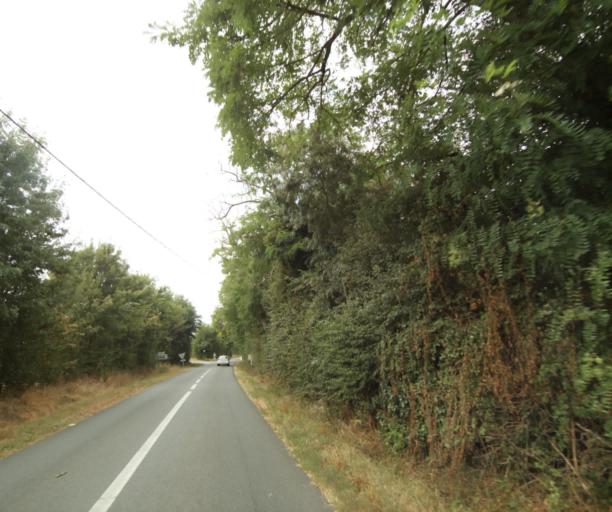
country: FR
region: Poitou-Charentes
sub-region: Departement de la Charente-Maritime
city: Tonnay-Charente
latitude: 45.9515
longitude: -0.8736
